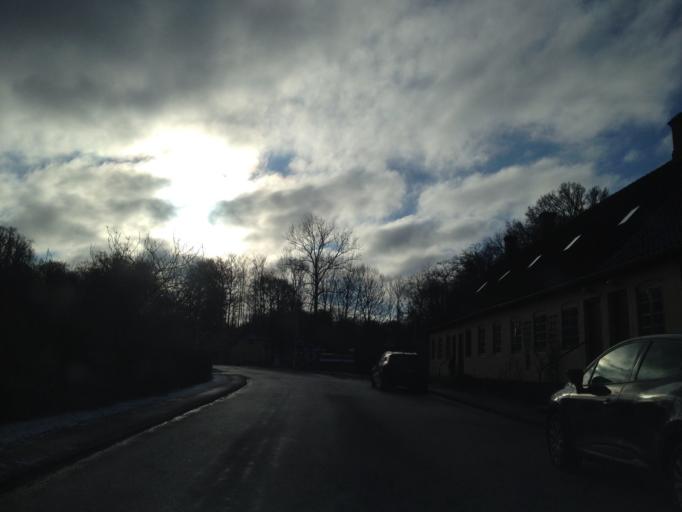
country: DK
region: Capital Region
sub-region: Helsingor Kommune
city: Hellebaek
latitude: 56.0678
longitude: 12.5537
